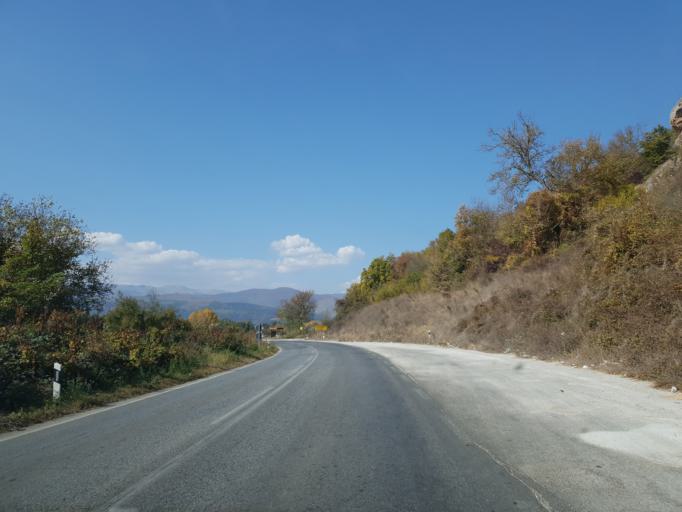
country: MK
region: Vranestica
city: Vranestica
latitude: 41.4806
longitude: 20.9953
